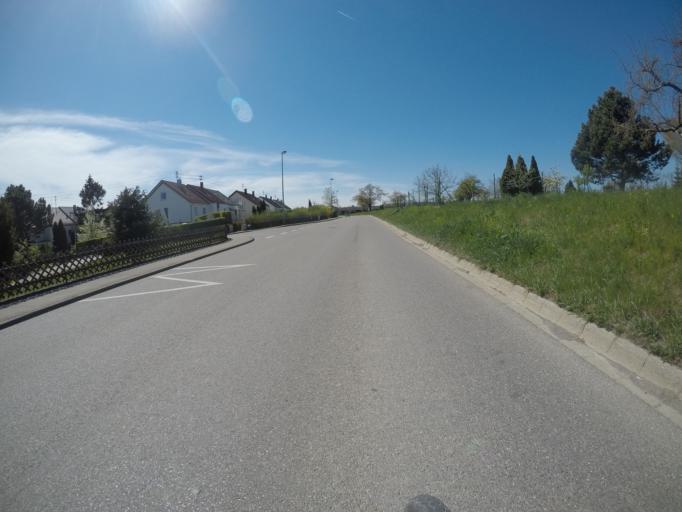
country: DE
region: Baden-Wuerttemberg
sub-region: Regierungsbezirk Stuttgart
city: Herrenberg
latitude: 48.5804
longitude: 8.8348
